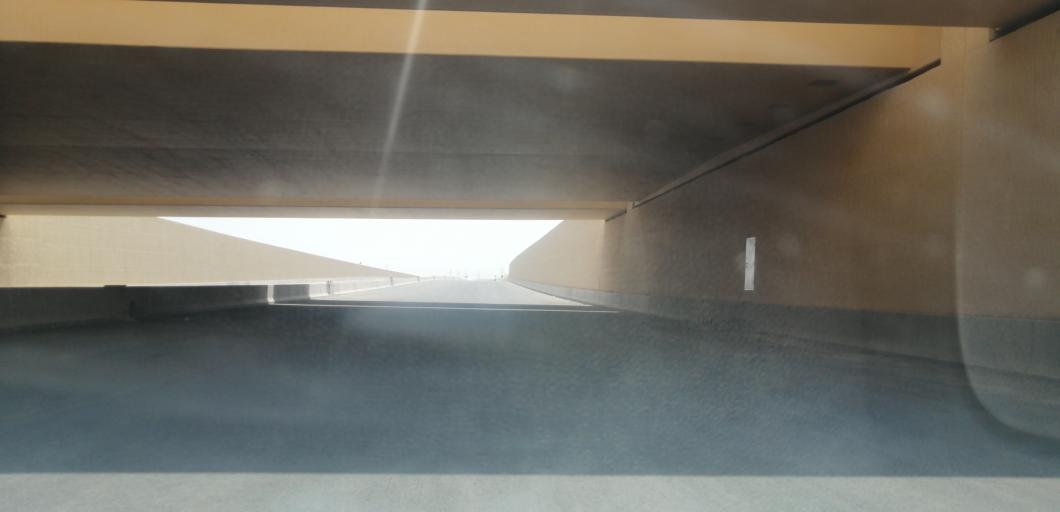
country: KW
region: Muhafazat al Jahra'
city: Al Jahra'
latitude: 29.4523
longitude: 47.5970
